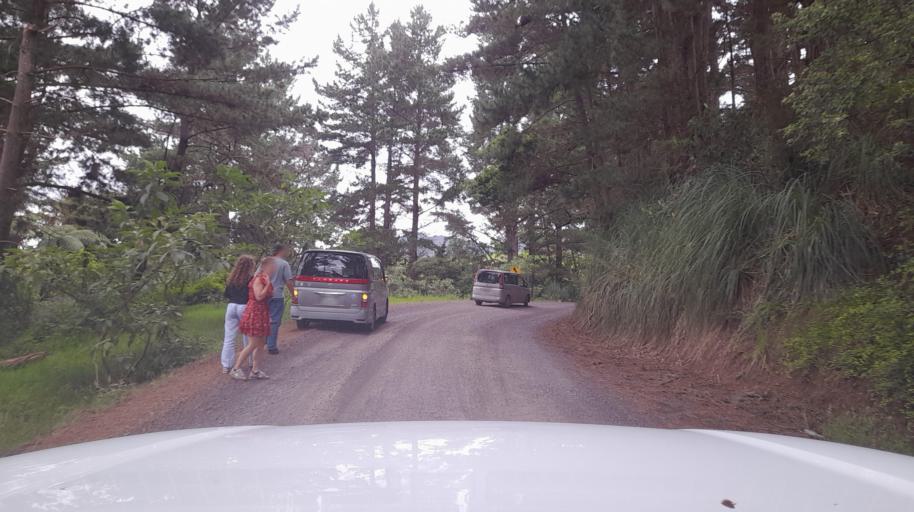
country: NZ
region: Northland
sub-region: Far North District
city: Kaitaia
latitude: -35.3134
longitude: 173.3422
